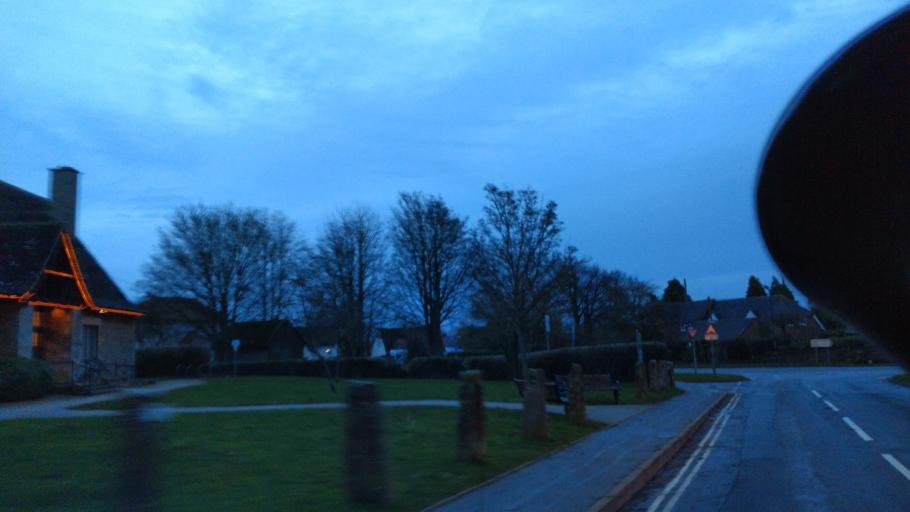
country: GB
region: England
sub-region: Oxfordshire
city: Shrivenham
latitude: 51.5980
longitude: -1.6586
